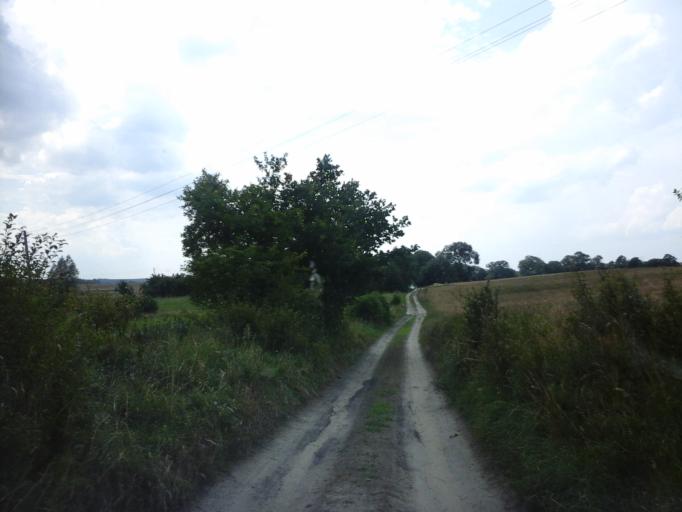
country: PL
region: West Pomeranian Voivodeship
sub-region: Powiat choszczenski
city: Bierzwnik
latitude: 53.0528
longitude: 15.6992
